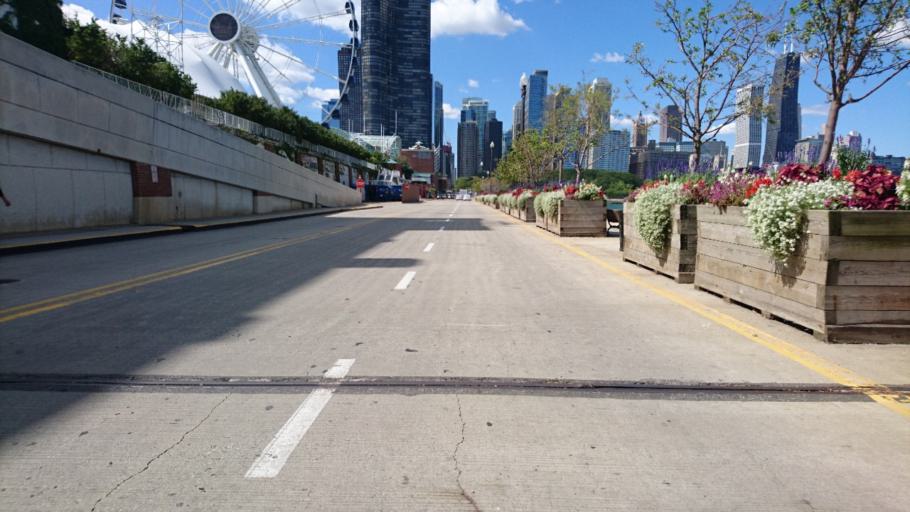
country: US
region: Illinois
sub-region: Cook County
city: Chicago
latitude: 41.8923
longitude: -87.6057
